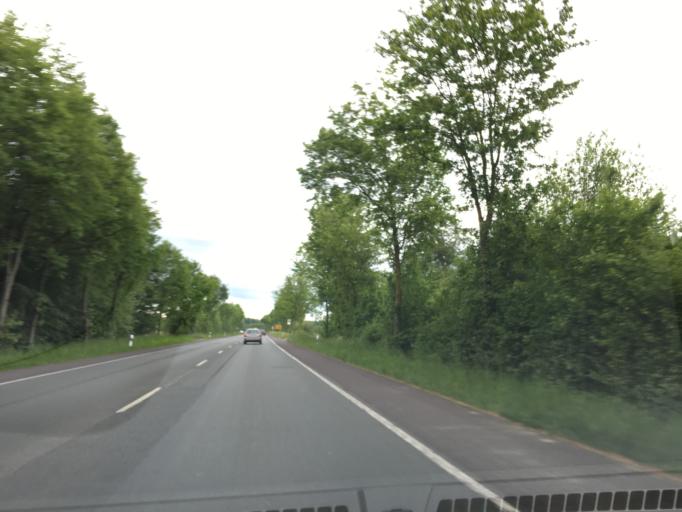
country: DE
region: North Rhine-Westphalia
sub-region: Regierungsbezirk Munster
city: Senden
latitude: 51.9156
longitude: 7.4852
